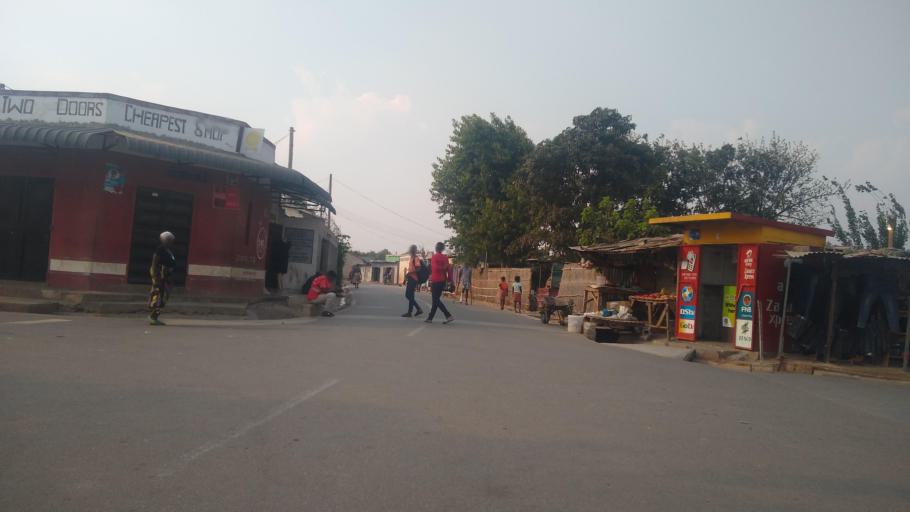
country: ZM
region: Lusaka
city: Lusaka
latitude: -15.4411
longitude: 28.3819
